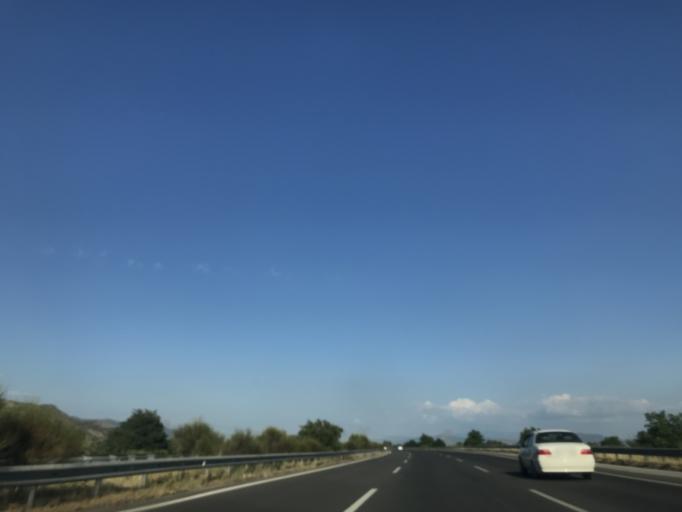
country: TR
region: Aydin
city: Incirliova
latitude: 37.8698
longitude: 27.7140
